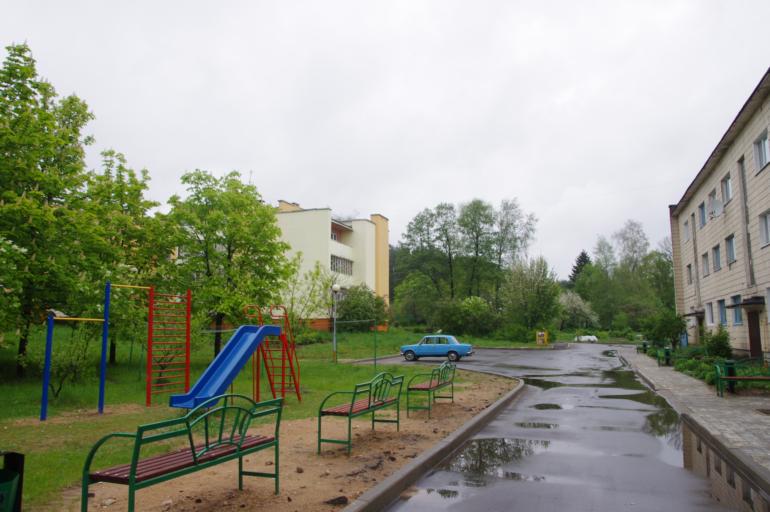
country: BY
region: Minsk
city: Narach
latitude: 54.9103
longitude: 26.7055
